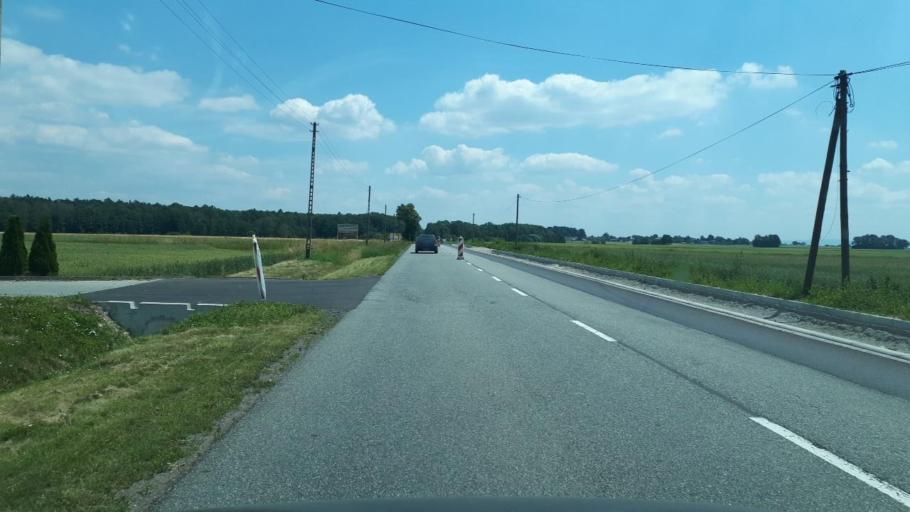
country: PL
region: Silesian Voivodeship
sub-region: Powiat pszczynski
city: Jankowice
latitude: 49.9711
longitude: 19.0010
